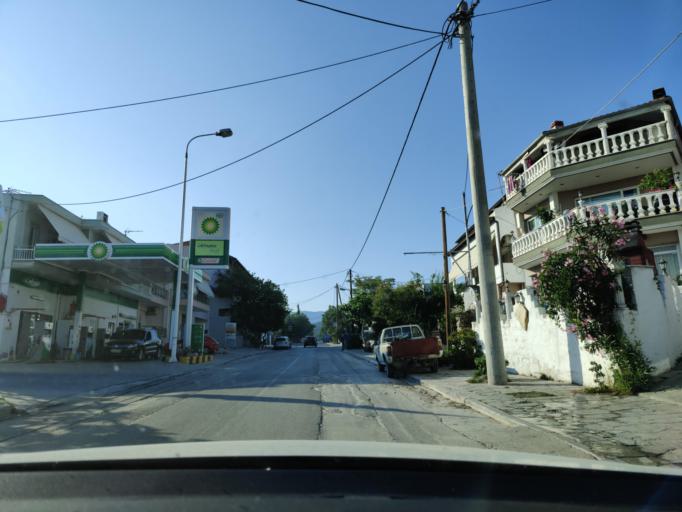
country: GR
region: East Macedonia and Thrace
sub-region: Nomos Kavalas
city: Limenaria
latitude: 40.6116
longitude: 24.6067
